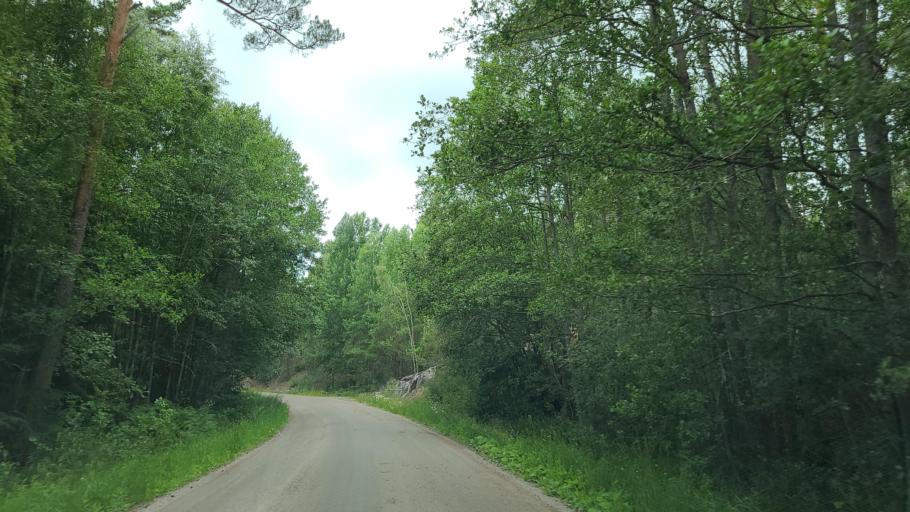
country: FI
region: Varsinais-Suomi
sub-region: Aboland-Turunmaa
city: Nagu
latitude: 60.2055
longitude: 21.8463
